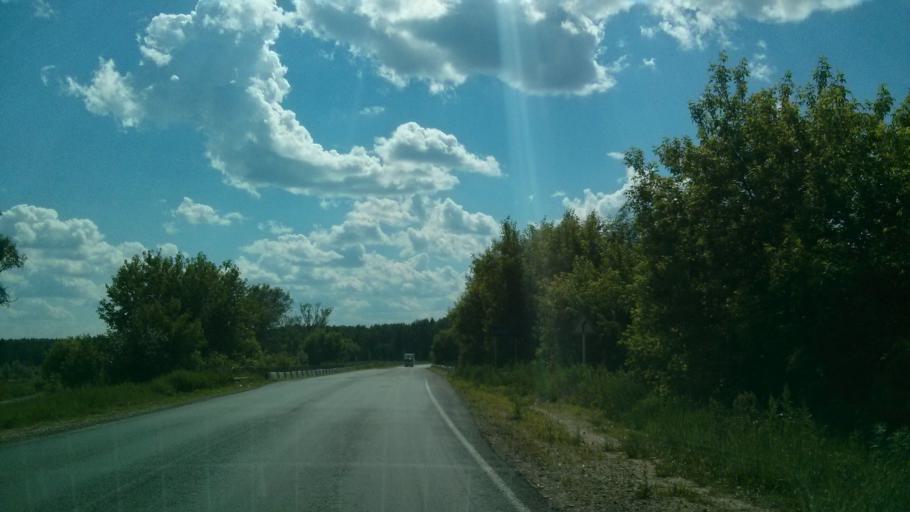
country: RU
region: Vladimir
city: Murom
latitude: 55.5242
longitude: 41.9524
